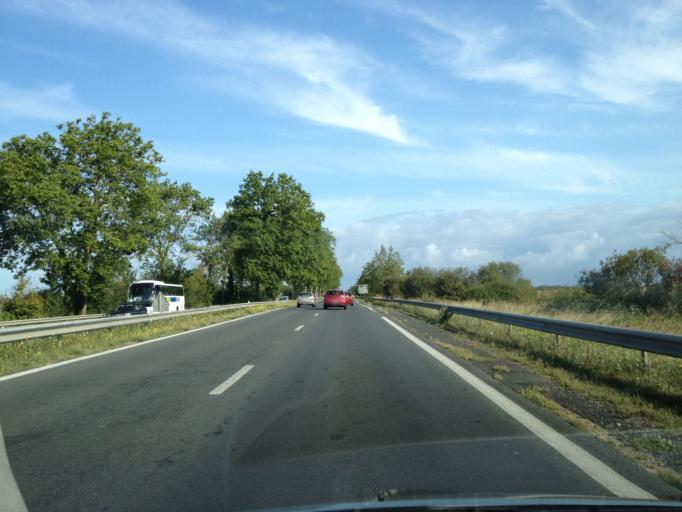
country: FR
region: Poitou-Charentes
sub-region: Departement de la Charente-Maritime
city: Yves
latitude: 46.0522
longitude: -1.0530
